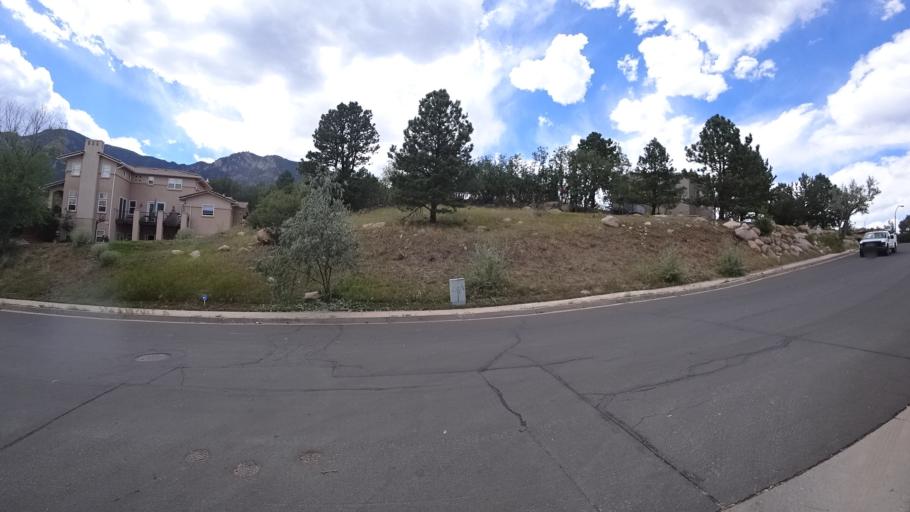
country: US
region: Colorado
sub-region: El Paso County
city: Stratmoor
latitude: 38.7721
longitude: -104.8312
